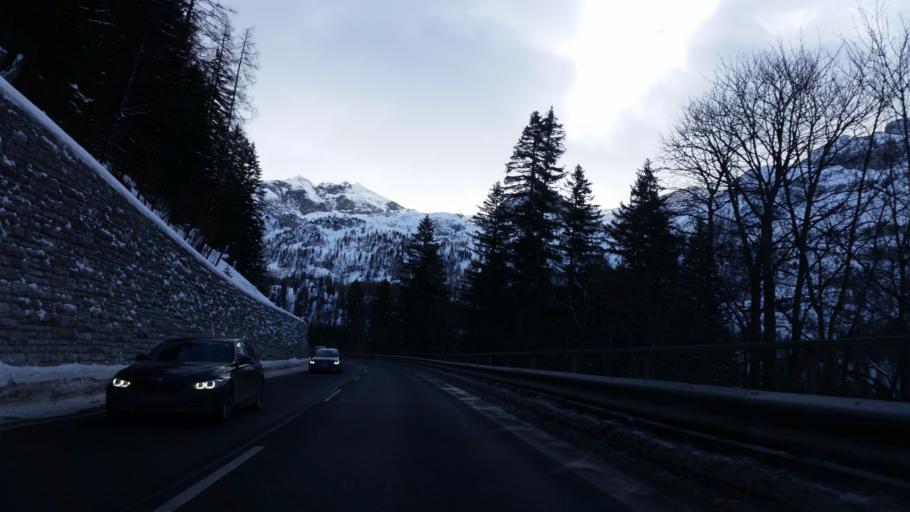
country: AT
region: Salzburg
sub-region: Politischer Bezirk Sankt Johann im Pongau
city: Untertauern
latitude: 47.2565
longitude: 13.4999
